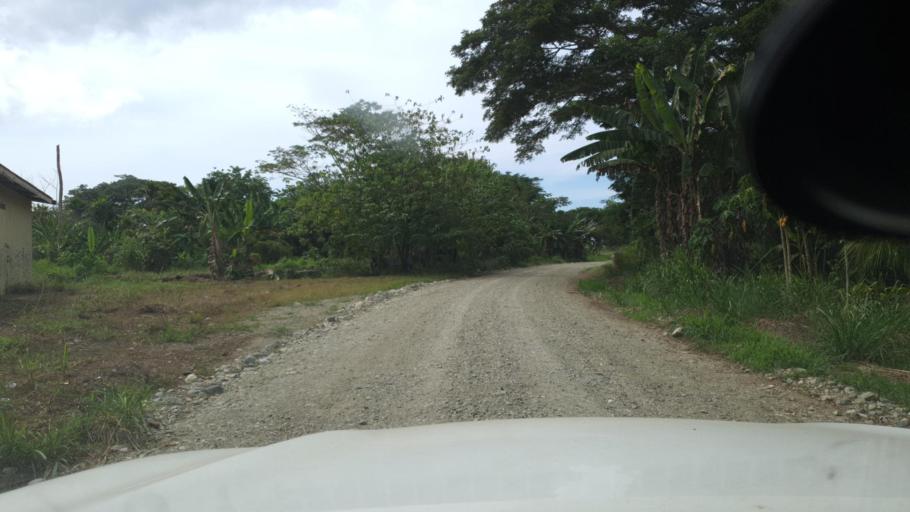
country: SB
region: Guadalcanal
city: Honiara
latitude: -9.4157
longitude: 159.8890
